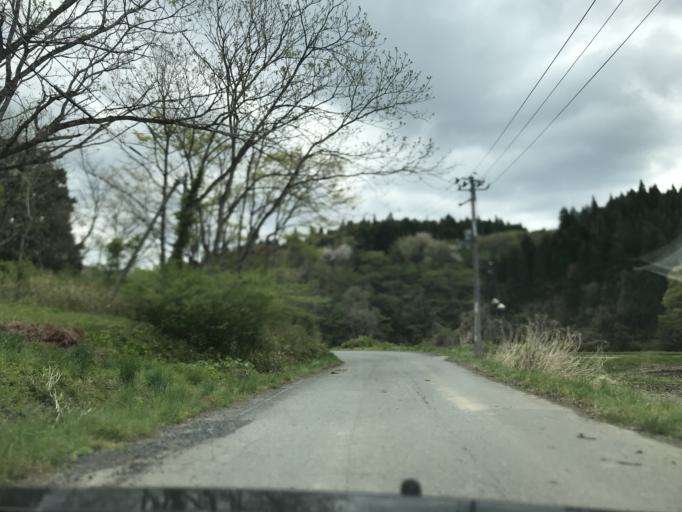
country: JP
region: Iwate
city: Ichinoseki
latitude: 38.8418
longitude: 141.3442
